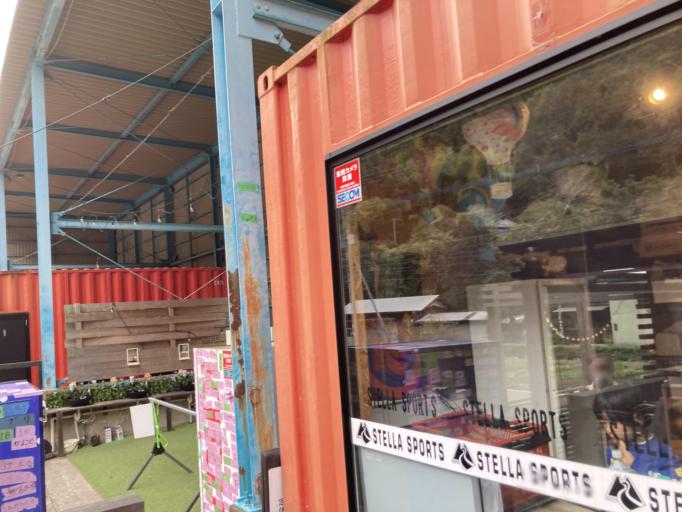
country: JP
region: Miyazaki
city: Tsuma
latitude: 32.2276
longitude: 131.1627
